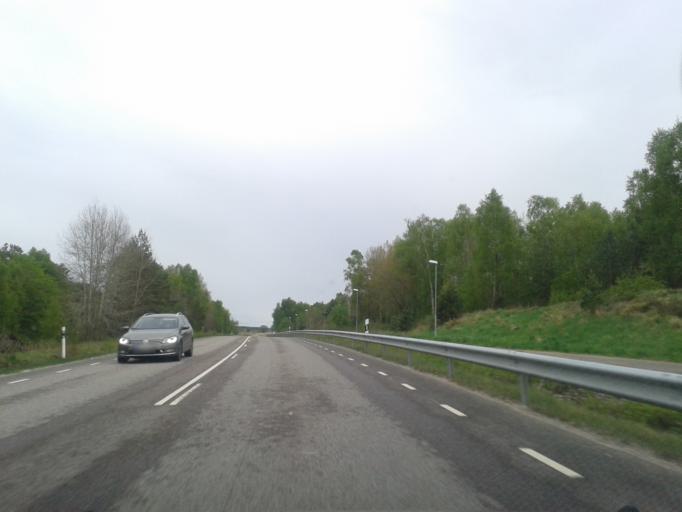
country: SE
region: Vaestra Goetaland
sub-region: Stenungsunds Kommun
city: Stora Hoga
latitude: 57.9986
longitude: 11.8265
